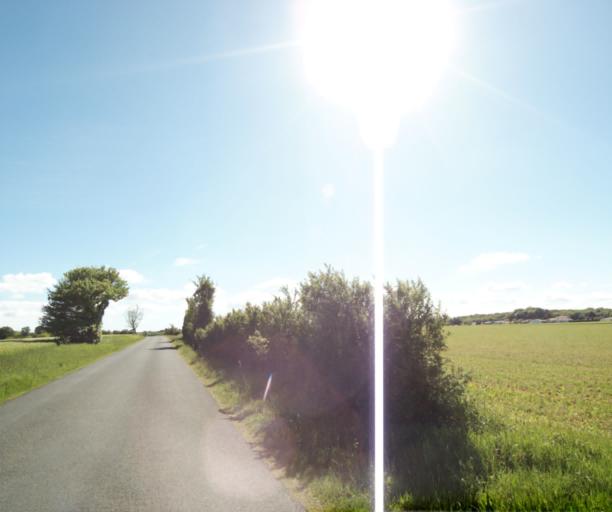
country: FR
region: Poitou-Charentes
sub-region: Departement de la Charente-Maritime
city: Bussac-sur-Charente
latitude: 45.8191
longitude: -0.6595
